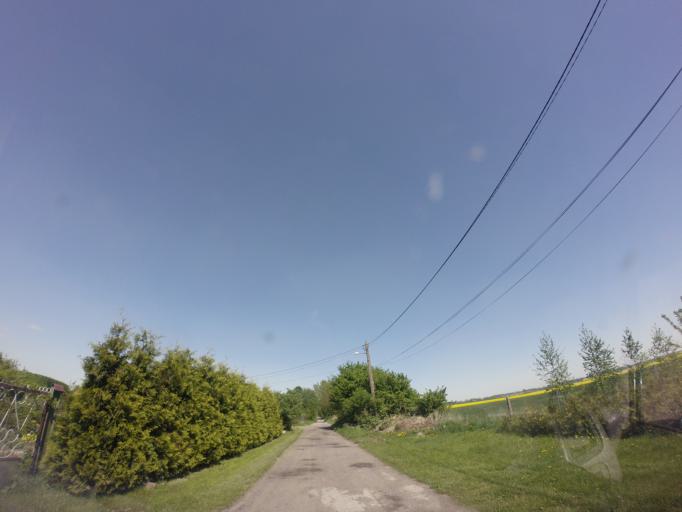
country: PL
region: West Pomeranian Voivodeship
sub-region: Powiat choszczenski
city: Pelczyce
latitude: 53.0181
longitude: 15.3455
